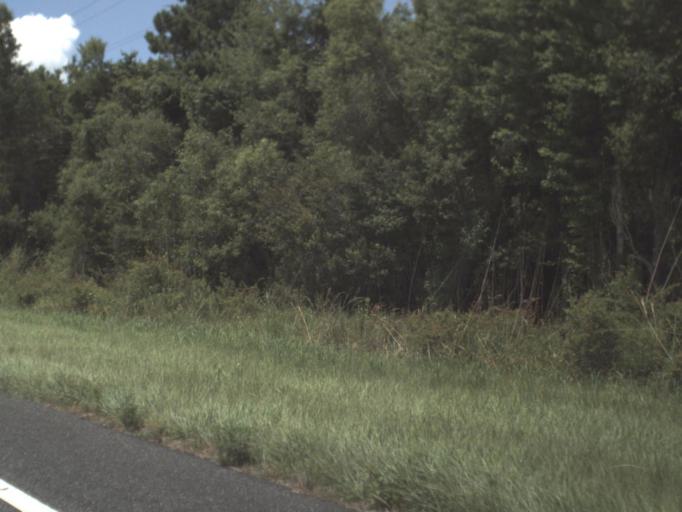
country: US
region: Florida
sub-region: Taylor County
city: Perry
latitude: 30.2642
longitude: -83.7126
